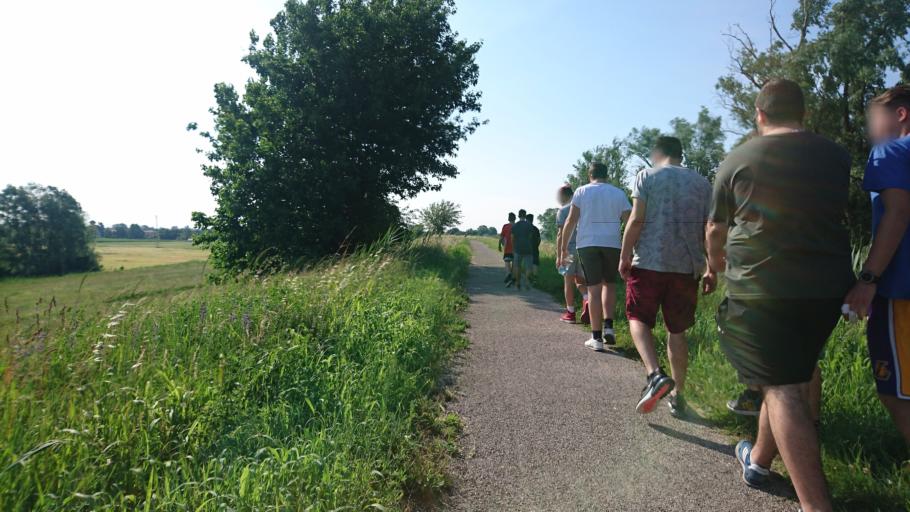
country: IT
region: Veneto
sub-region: Provincia di Verona
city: Boschi Sant'Anna
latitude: 45.1903
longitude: 11.3191
